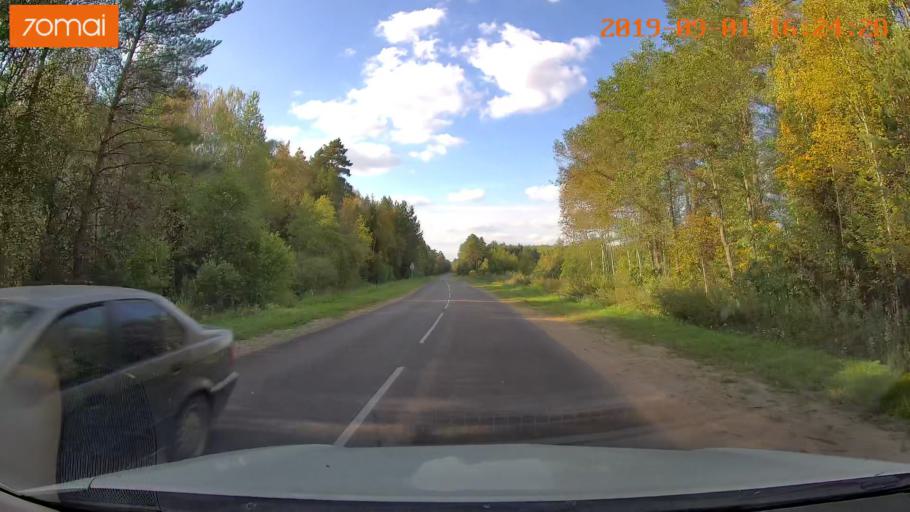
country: RU
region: Kaluga
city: Maloyaroslavets
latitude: 54.8905
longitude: 36.5223
